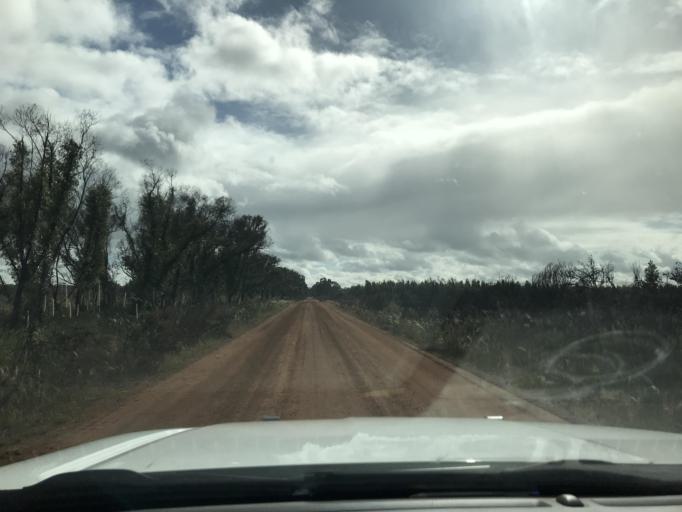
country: AU
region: South Australia
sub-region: Wattle Range
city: Penola
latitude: -37.1892
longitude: 141.1883
